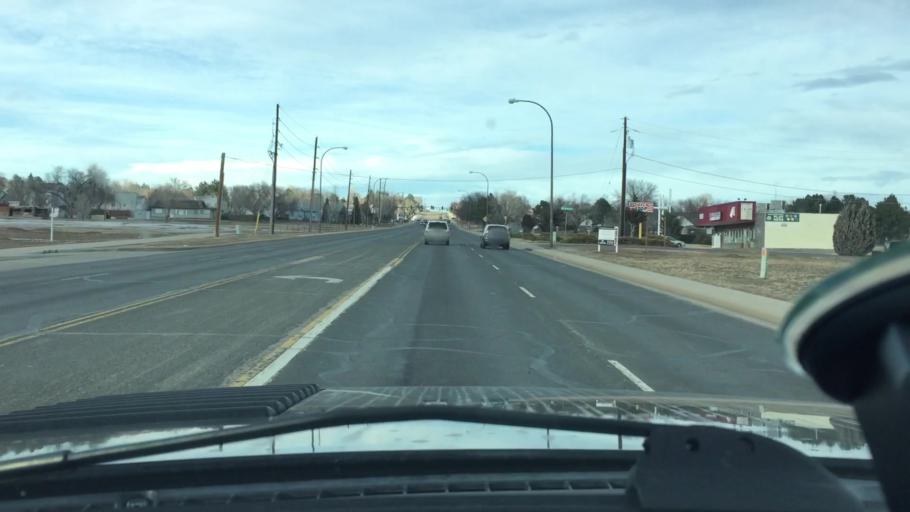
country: US
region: Colorado
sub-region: Adams County
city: Federal Heights
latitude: 39.8683
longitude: -104.9966
